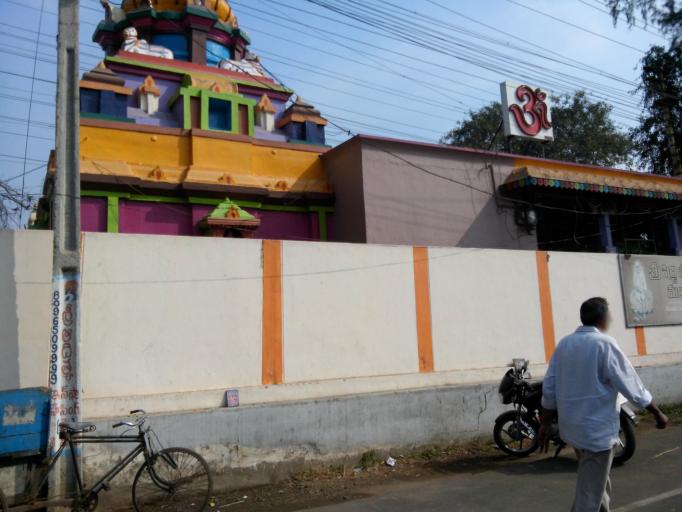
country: IN
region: Andhra Pradesh
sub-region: Krishna
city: Vijayawada
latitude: 16.5232
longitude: 80.6659
